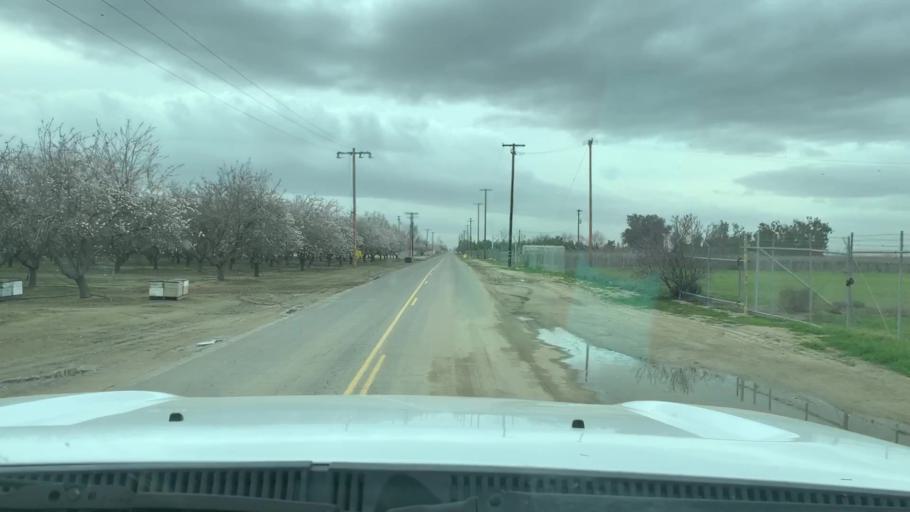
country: US
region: California
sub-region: Kern County
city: Shafter
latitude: 35.5292
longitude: -119.2606
